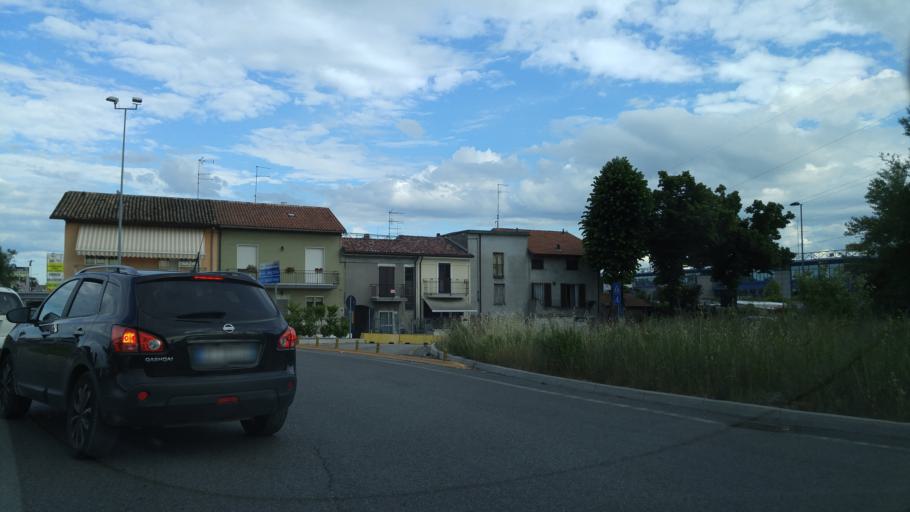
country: IT
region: Emilia-Romagna
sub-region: Provincia di Rimini
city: Rimini
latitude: 44.0439
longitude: 12.5595
